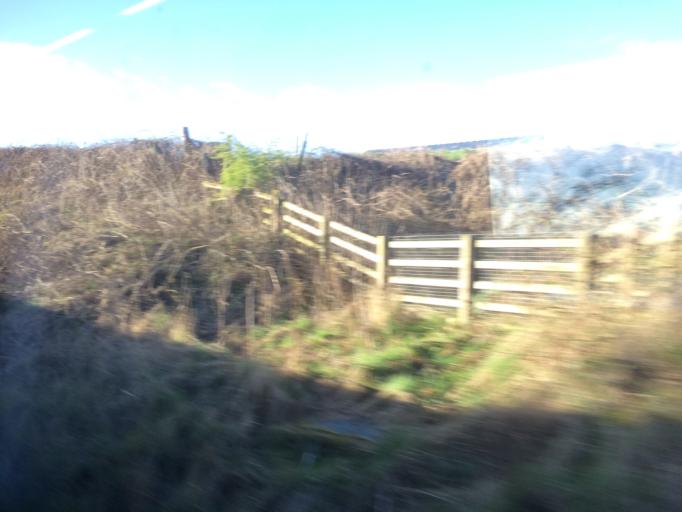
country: GB
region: Scotland
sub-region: Stirling
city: Bannockburn
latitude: 56.0874
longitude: -3.8885
